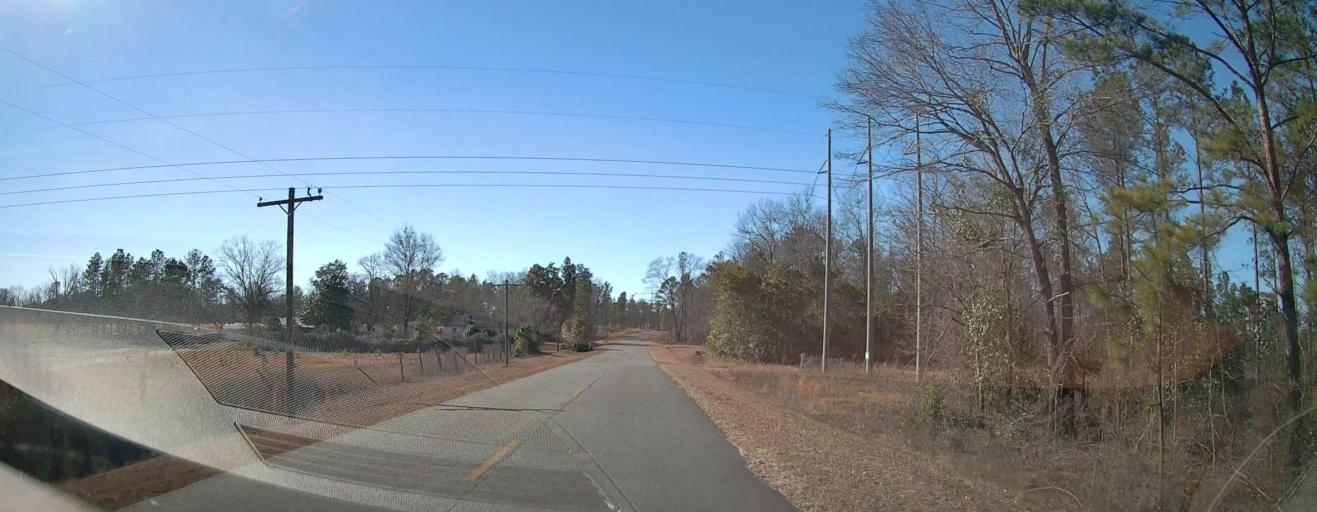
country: US
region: Georgia
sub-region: Taylor County
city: Butler
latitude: 32.6381
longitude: -84.2949
